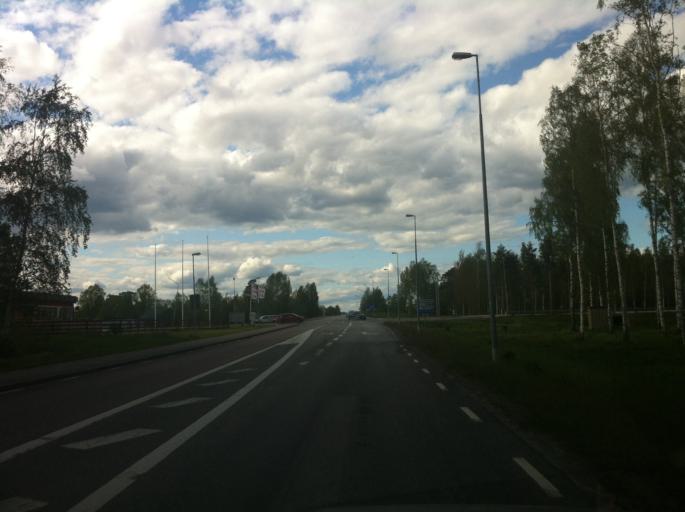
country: SE
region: Vaermland
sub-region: Storfors Kommun
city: Storfors
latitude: 59.5353
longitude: 14.2824
